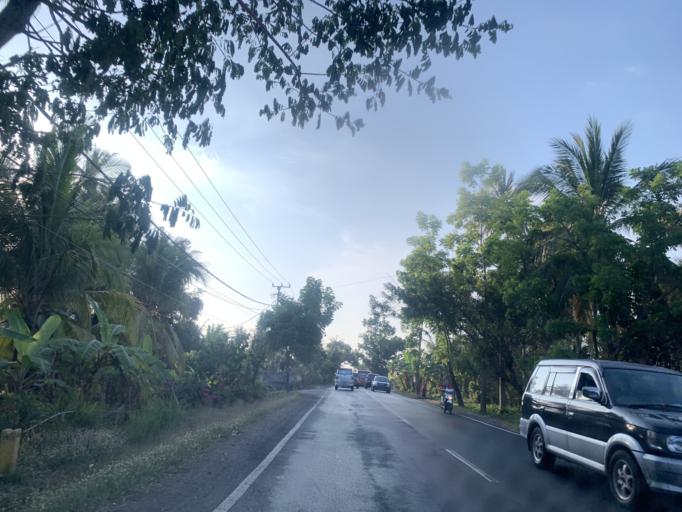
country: ID
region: Bali
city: Banjar Delodrurung
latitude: -8.4918
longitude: 114.9568
